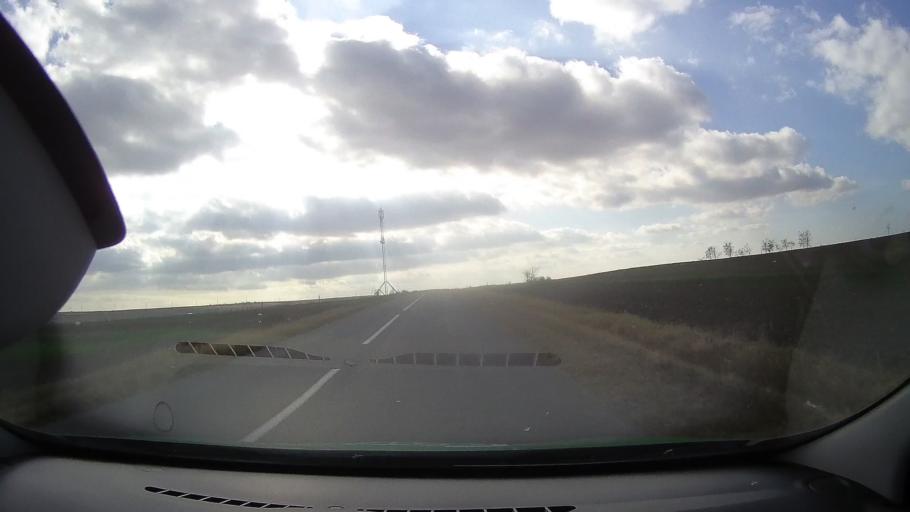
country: RO
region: Constanta
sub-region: Comuna Sacele
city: Sacele
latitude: 44.4934
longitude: 28.6554
